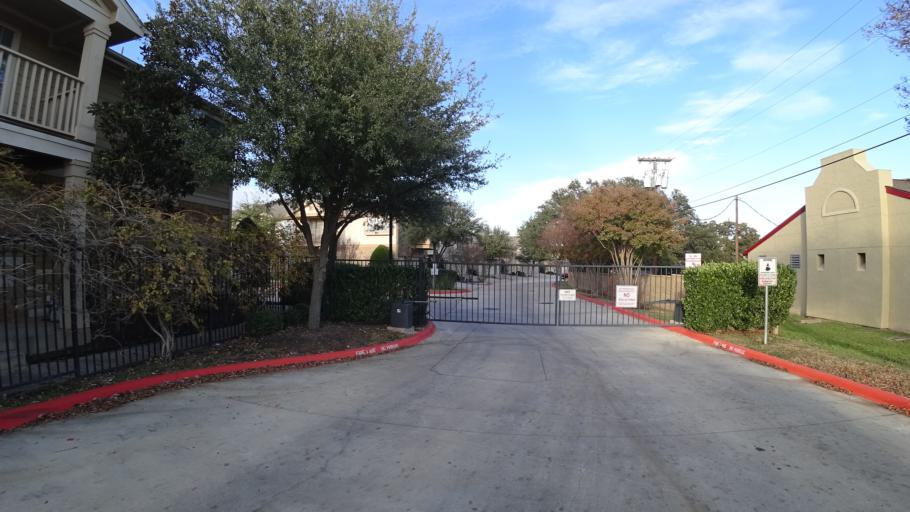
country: US
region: Texas
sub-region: Williamson County
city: Brushy Creek
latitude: 30.4948
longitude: -97.7277
